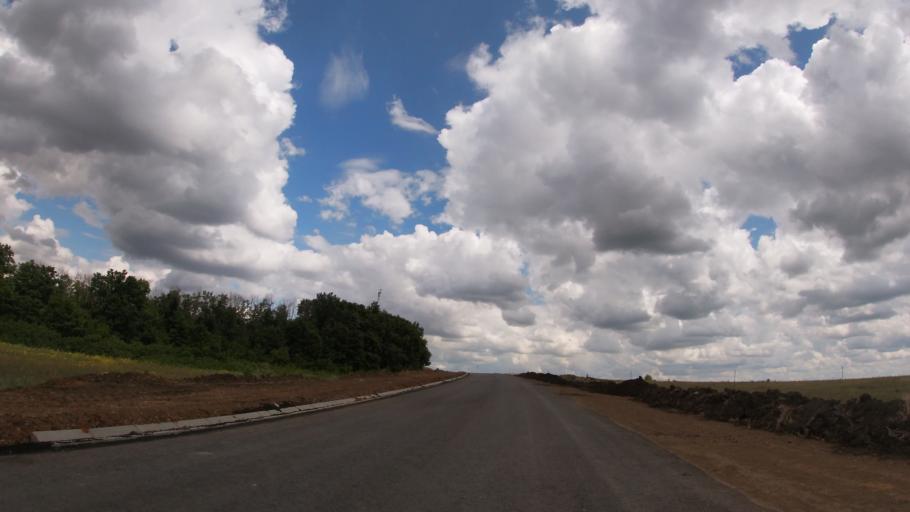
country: RU
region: Belgorod
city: Mayskiy
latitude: 50.5206
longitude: 36.5034
